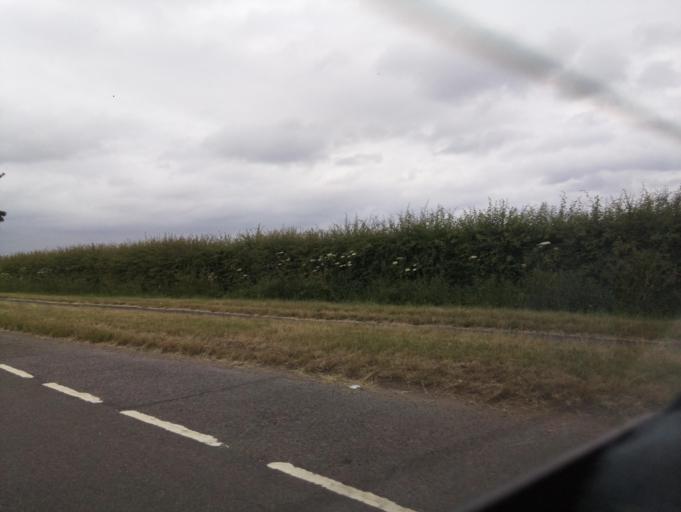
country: GB
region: England
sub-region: Staffordshire
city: Penkridge
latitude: 52.7389
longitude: -2.1098
